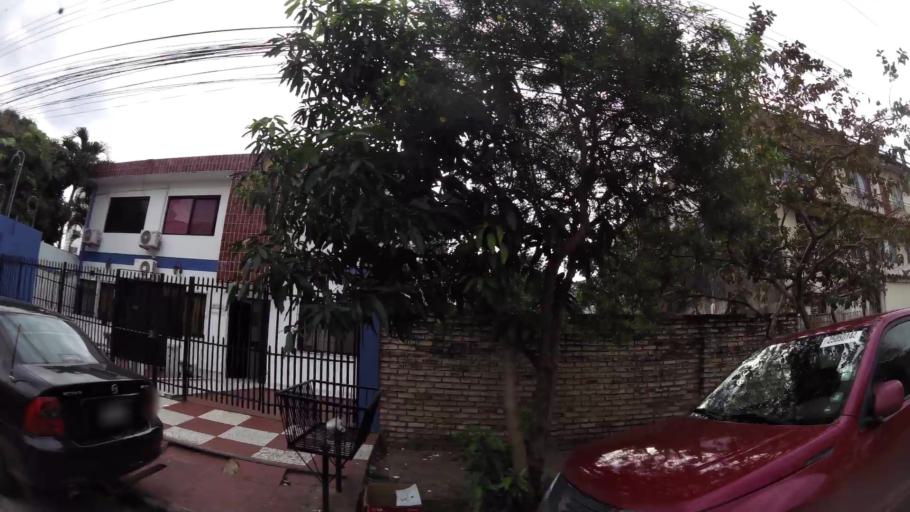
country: BO
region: Santa Cruz
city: Santa Cruz de la Sierra
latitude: -17.7746
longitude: -63.1898
